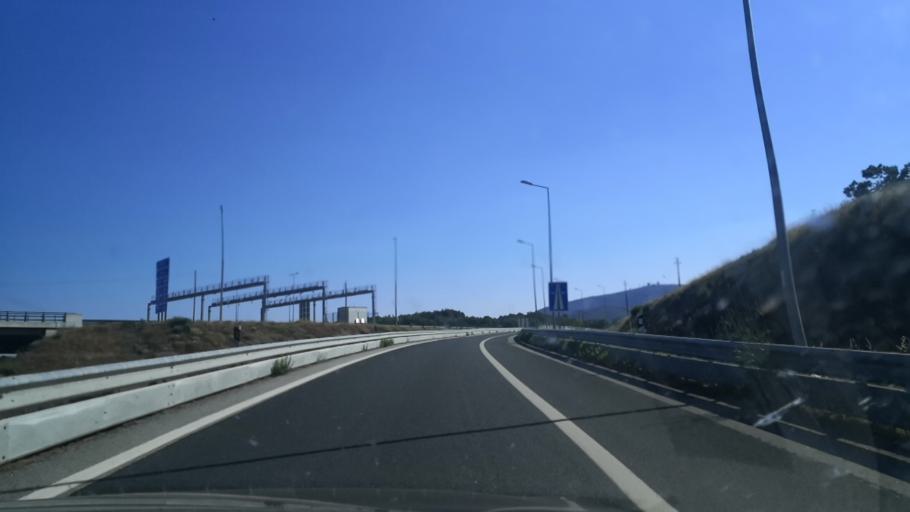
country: PT
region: Braganca
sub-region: Braganca Municipality
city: Braganca
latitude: 41.7638
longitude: -6.7927
